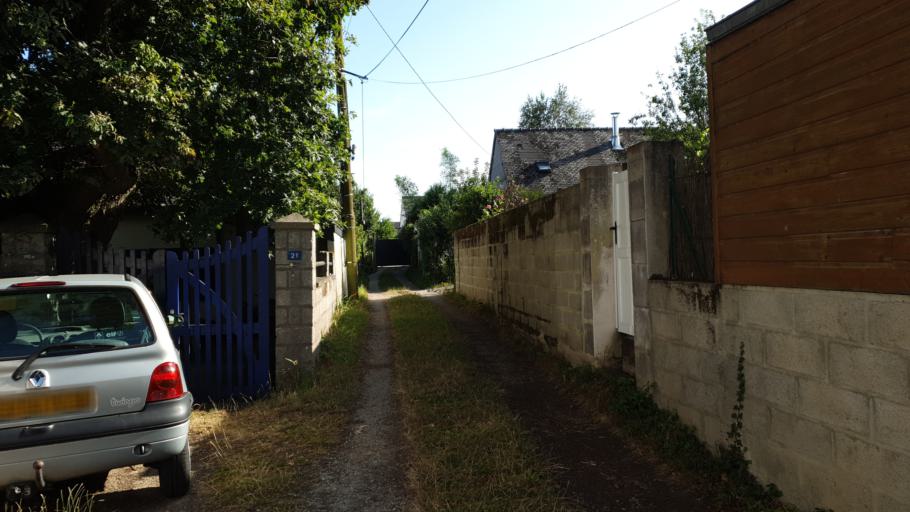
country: FR
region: Brittany
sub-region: Departement du Morbihan
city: Vannes
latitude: 47.6417
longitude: -2.7636
